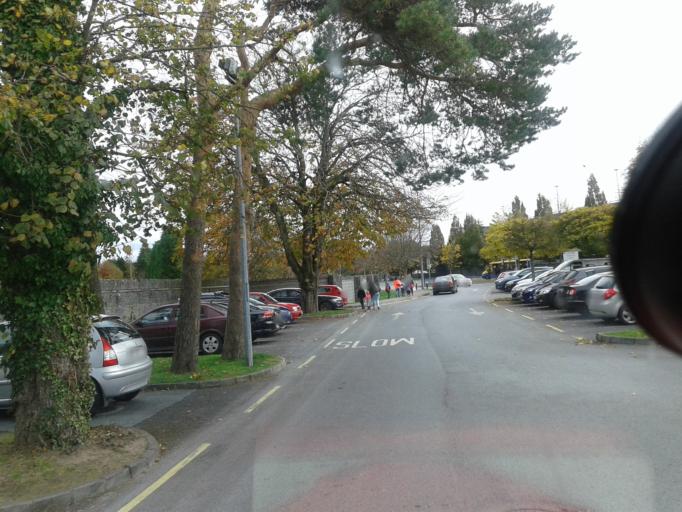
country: IE
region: Munster
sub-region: An Clar
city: Ennis
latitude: 52.8440
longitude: -8.9808
